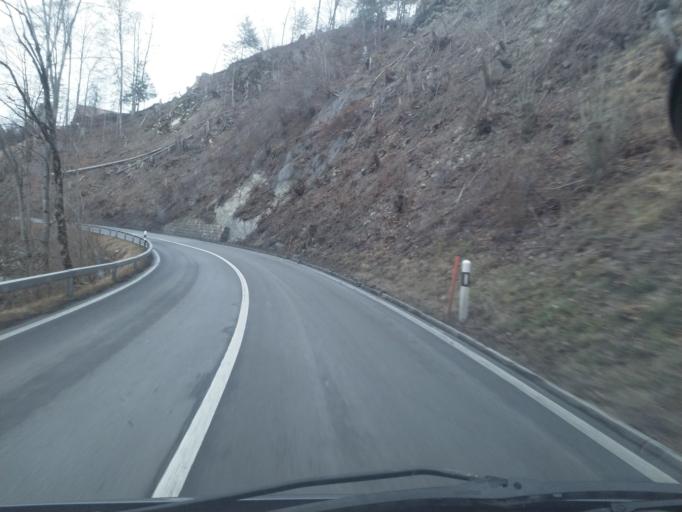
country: CH
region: Bern
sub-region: Frutigen-Niedersimmental District
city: Erlenbach im Simmental
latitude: 46.6580
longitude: 7.4724
